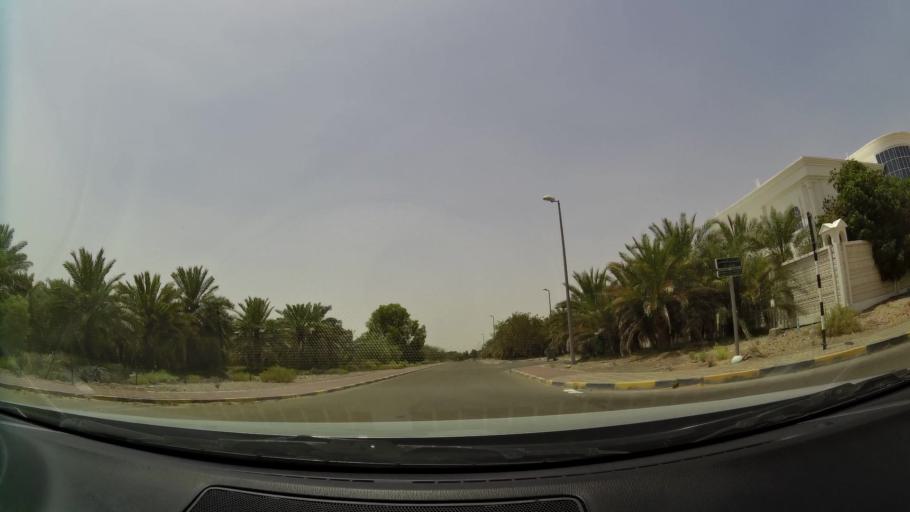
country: AE
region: Abu Dhabi
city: Al Ain
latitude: 24.1984
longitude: 55.7056
